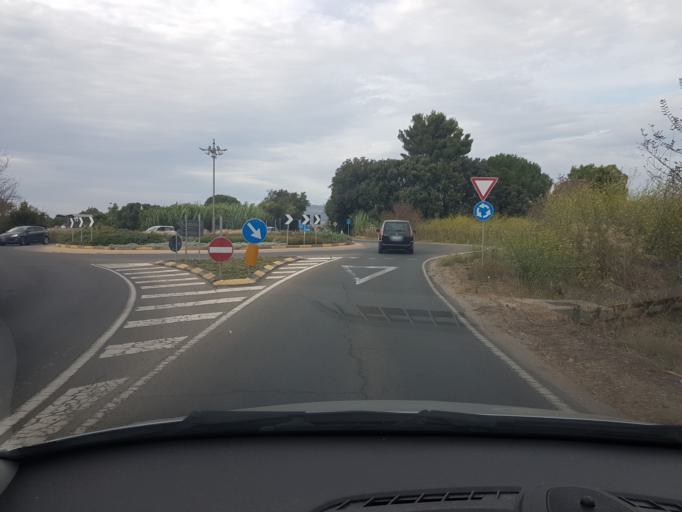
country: IT
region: Sardinia
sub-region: Provincia di Oristano
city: Nurachi
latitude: 39.9819
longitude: 8.5393
